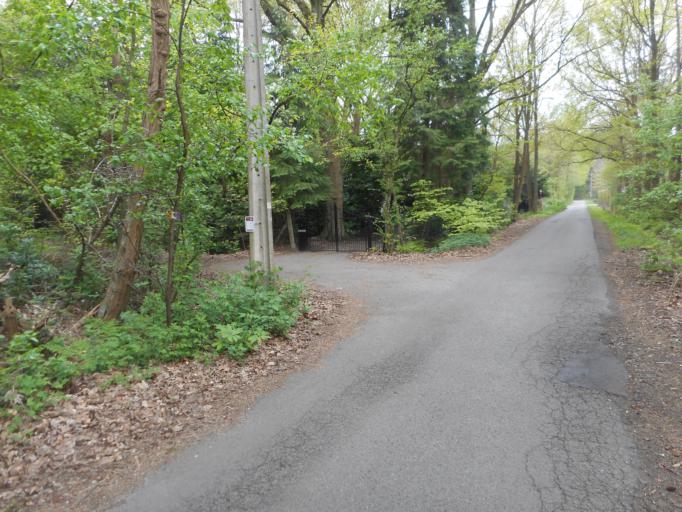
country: BE
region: Flanders
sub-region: Provincie Antwerpen
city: Zandhoven
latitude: 51.2327
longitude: 4.6795
